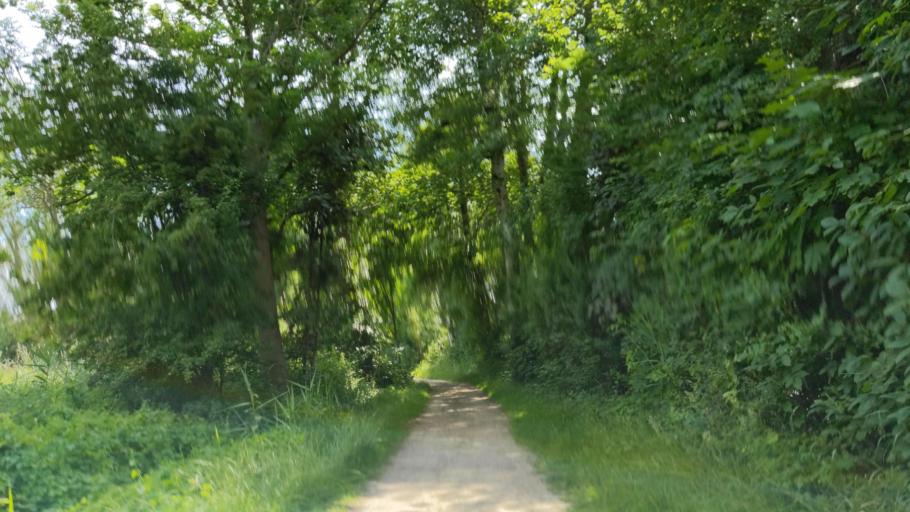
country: DE
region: Schleswig-Holstein
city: Eutin
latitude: 54.1384
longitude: 10.6354
